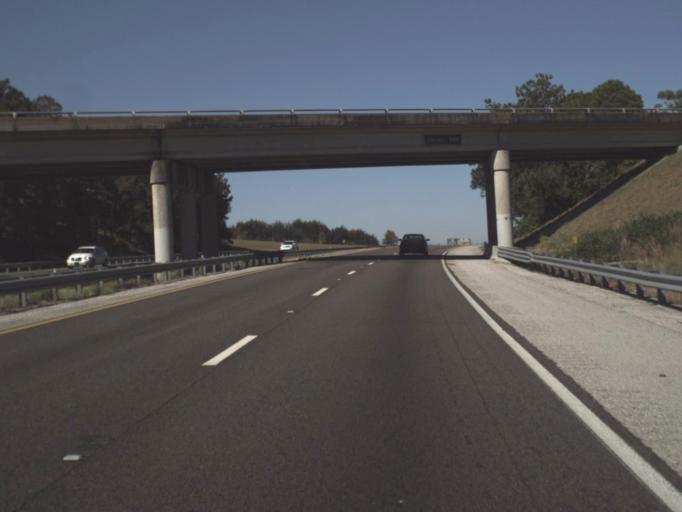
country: US
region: Florida
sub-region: Lake County
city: Montverde
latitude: 28.5608
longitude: -81.6817
